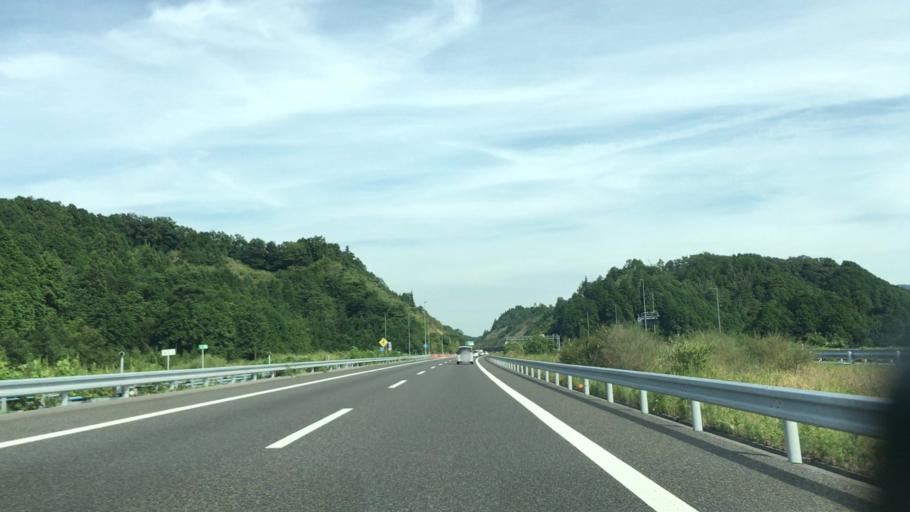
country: JP
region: Shiga Prefecture
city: Hino
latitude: 34.9235
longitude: 136.2643
